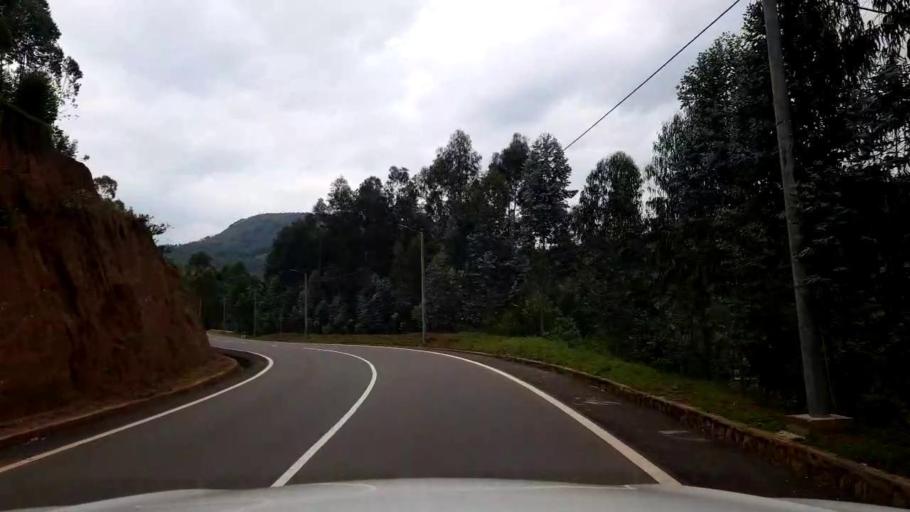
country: RW
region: Western Province
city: Kibuye
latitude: -1.9230
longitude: 29.3689
